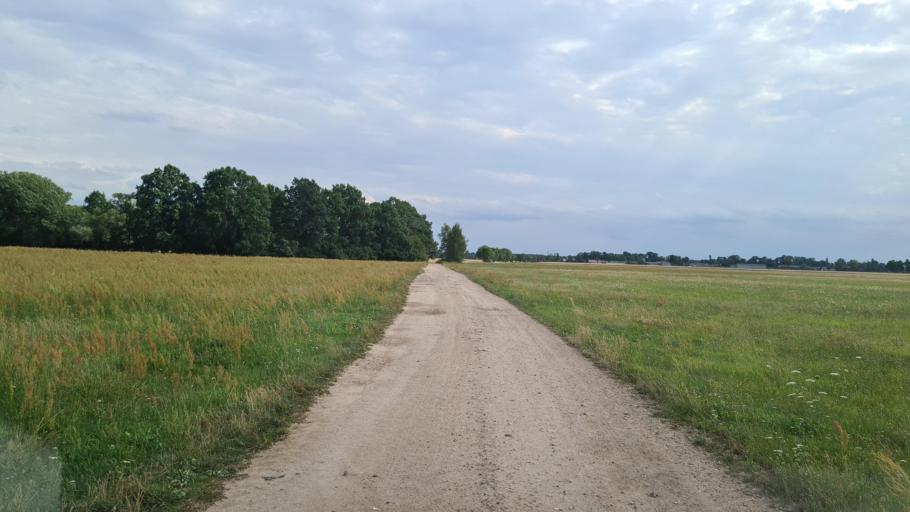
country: DE
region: Saxony-Anhalt
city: Holzdorf
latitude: 51.8109
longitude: 13.1821
